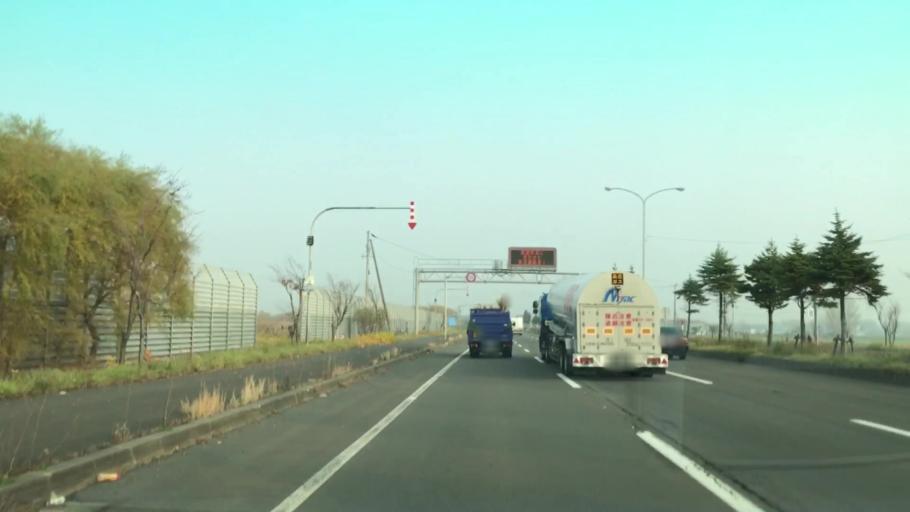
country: JP
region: Hokkaido
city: Ishikari
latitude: 43.1714
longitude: 141.3484
